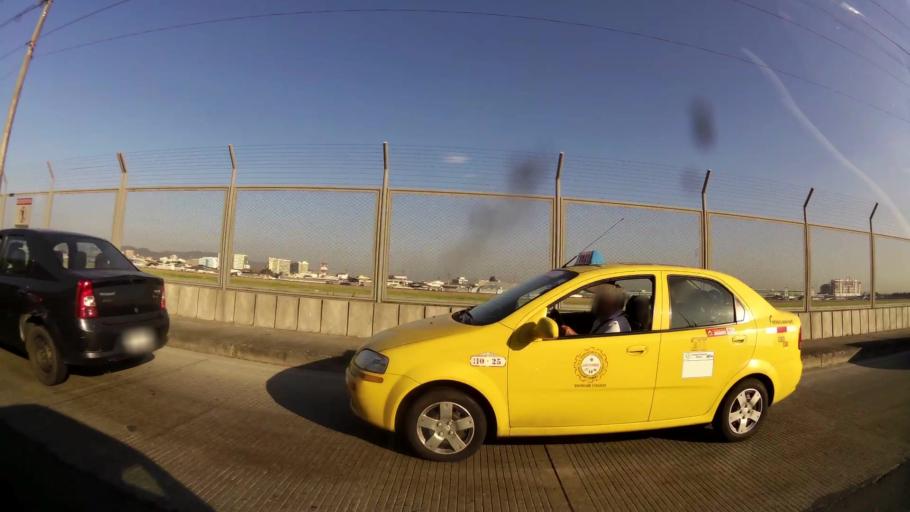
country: EC
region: Guayas
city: Eloy Alfaro
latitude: -2.1555
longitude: -79.8800
